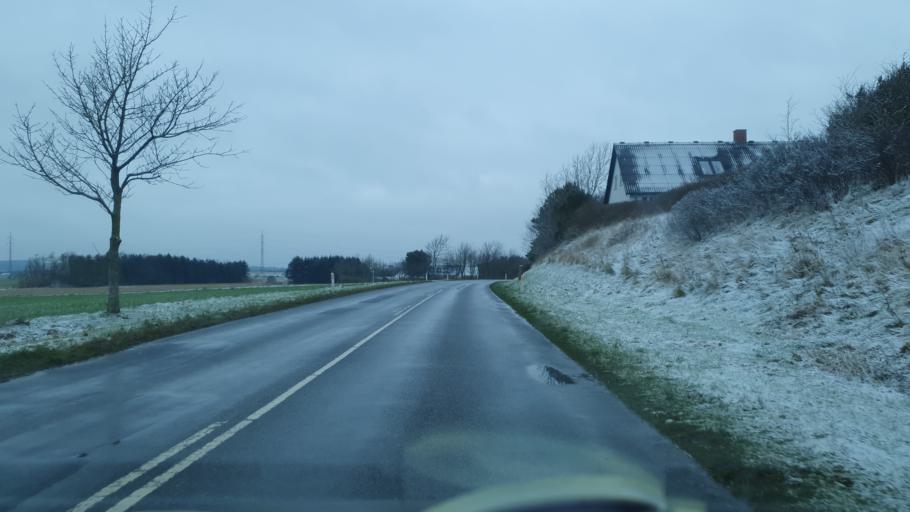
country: DK
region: North Denmark
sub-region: Jammerbugt Kommune
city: Brovst
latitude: 57.1093
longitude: 9.5010
